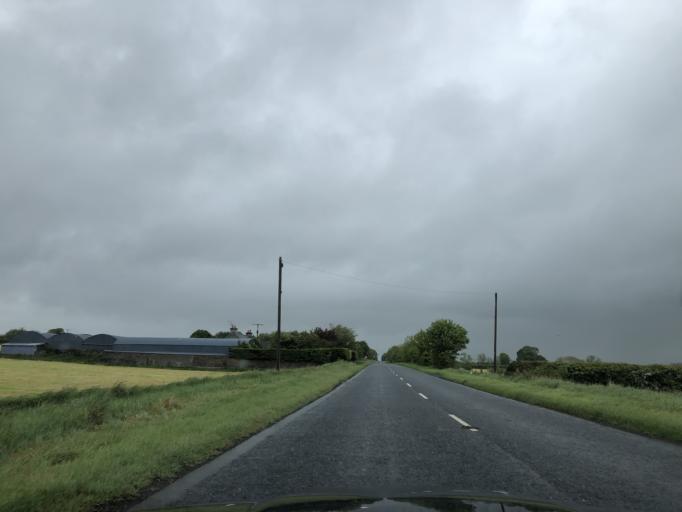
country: GB
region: Northern Ireland
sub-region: Moyle District
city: Ballycastle
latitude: 55.1749
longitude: -6.3369
